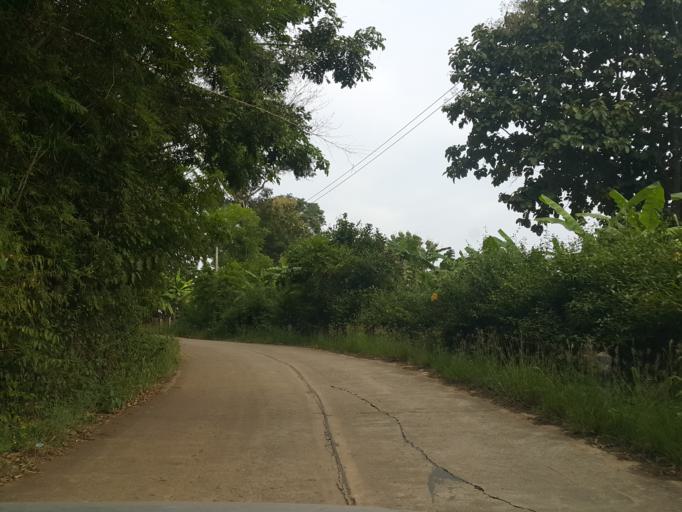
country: TH
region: Mae Hong Son
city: Wiang Nuea
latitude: 19.3682
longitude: 98.4498
